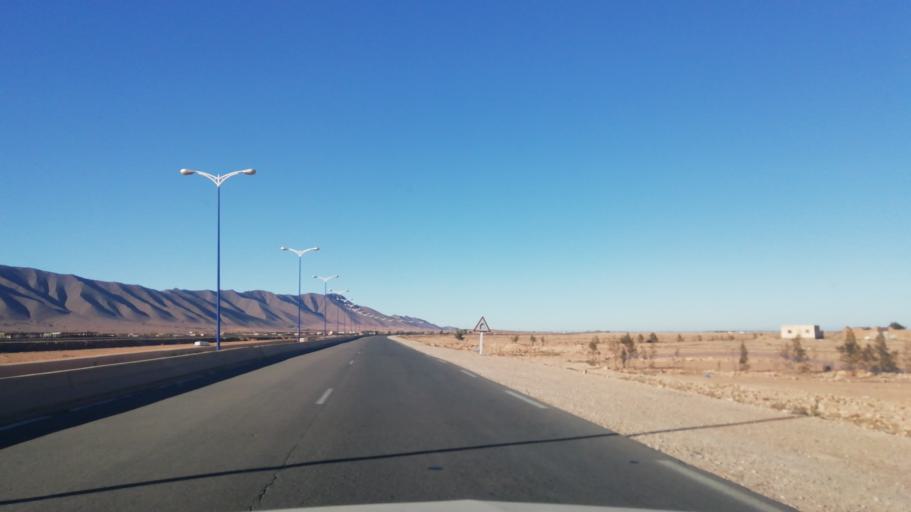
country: DZ
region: Wilaya de Naama
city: Naama
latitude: 33.5649
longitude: -0.2391
